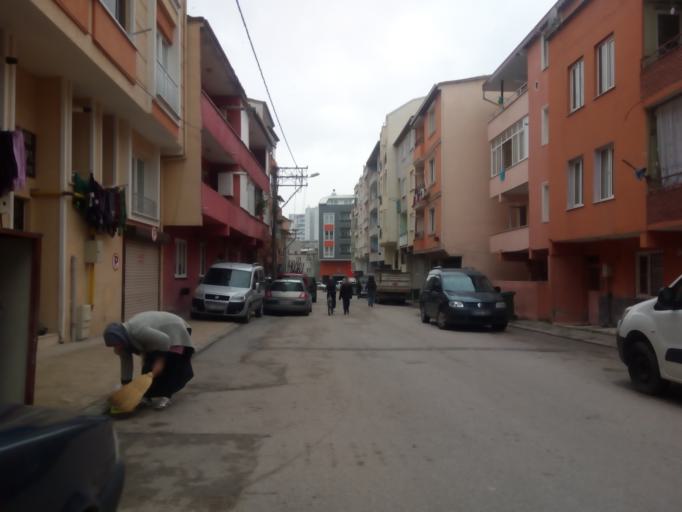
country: TR
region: Bursa
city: Niluefer
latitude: 40.2562
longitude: 28.9611
